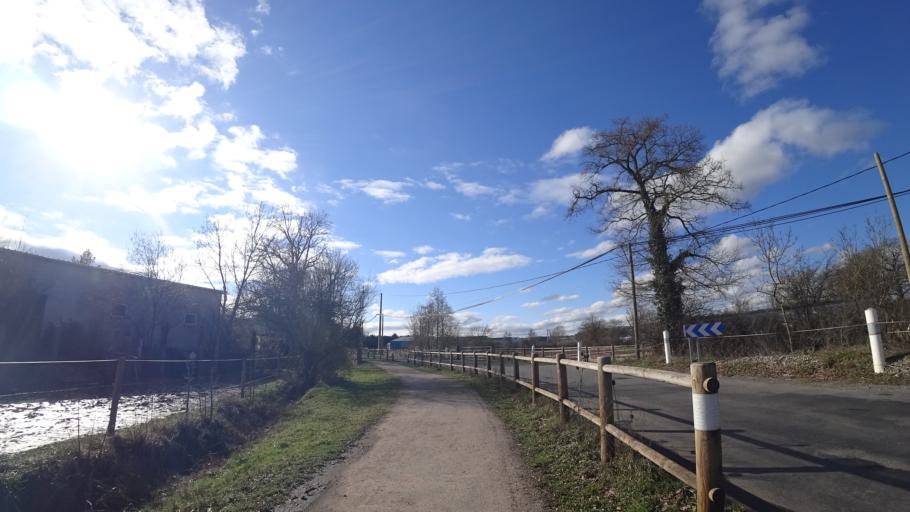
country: FR
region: Midi-Pyrenees
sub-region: Departement de l'Aveyron
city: Rodez
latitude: 44.3729
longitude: 2.5964
